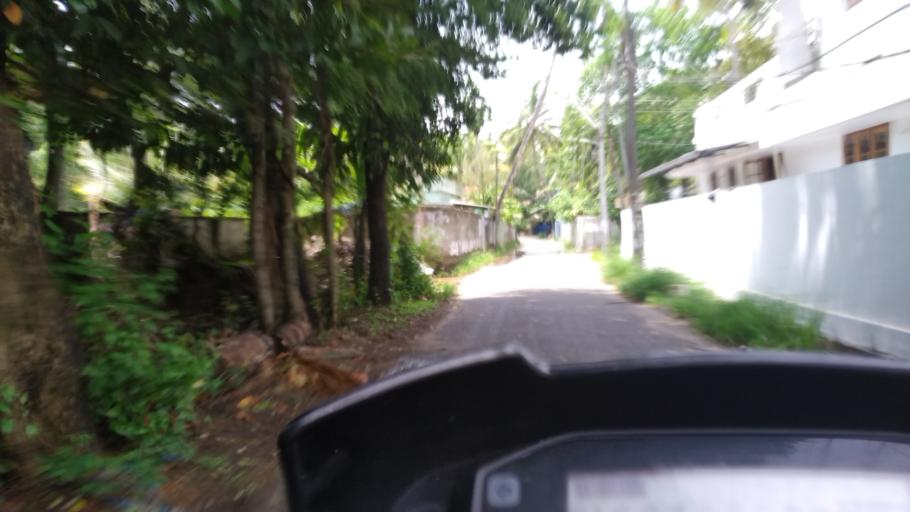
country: IN
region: Kerala
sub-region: Ernakulam
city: Elur
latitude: 10.0853
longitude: 76.2044
